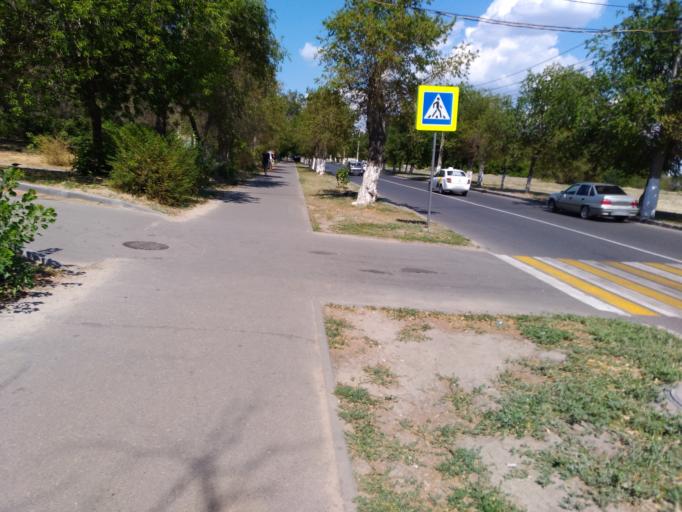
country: RU
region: Volgograd
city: Volgograd
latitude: 48.7163
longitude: 44.5153
